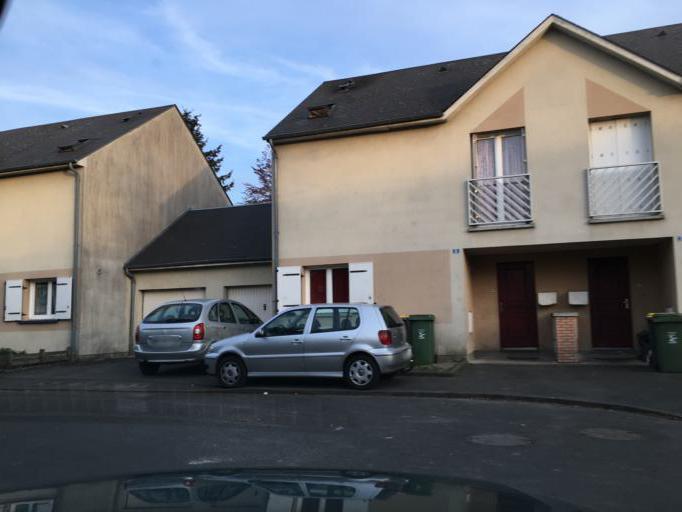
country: FR
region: Centre
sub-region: Departement du Loiret
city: Orleans
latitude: 47.9195
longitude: 1.8909
